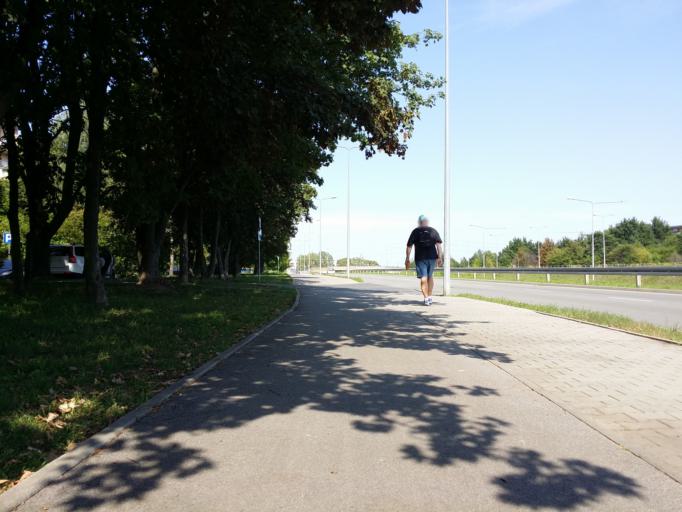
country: PL
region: Masovian Voivodeship
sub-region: Radom
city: Radom
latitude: 51.3735
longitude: 21.1642
